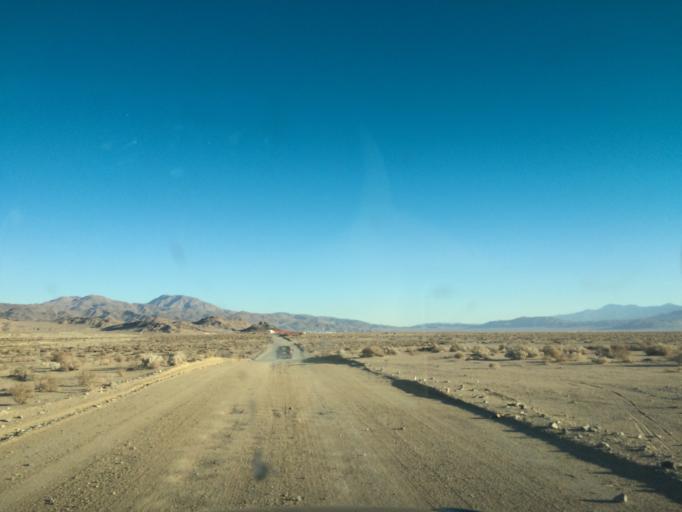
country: US
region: California
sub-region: San Bernardino County
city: Searles Valley
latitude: 35.6656
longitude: -117.3789
